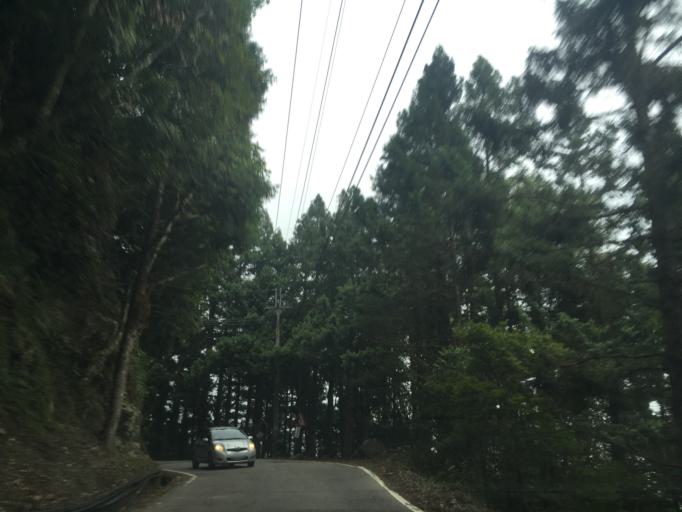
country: TW
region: Taiwan
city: Fengyuan
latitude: 24.2446
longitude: 120.9205
